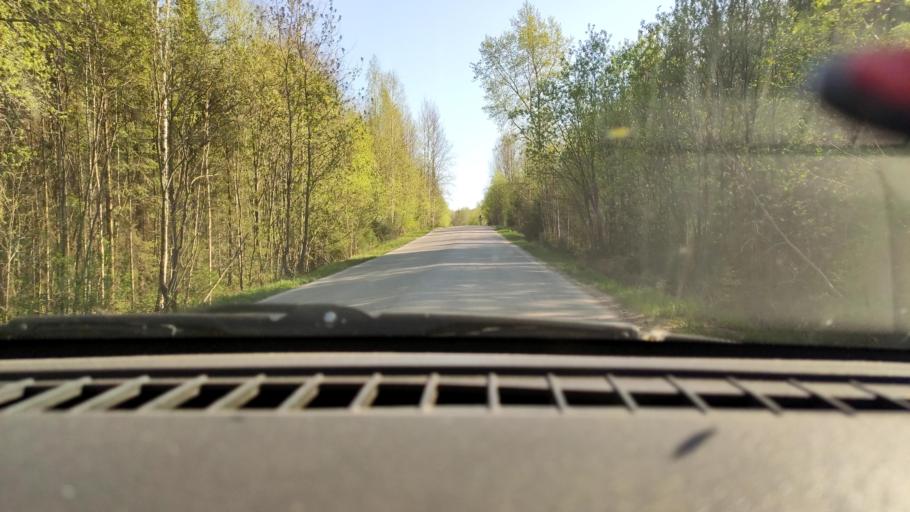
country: RU
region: Perm
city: Overyata
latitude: 58.0750
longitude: 56.0016
